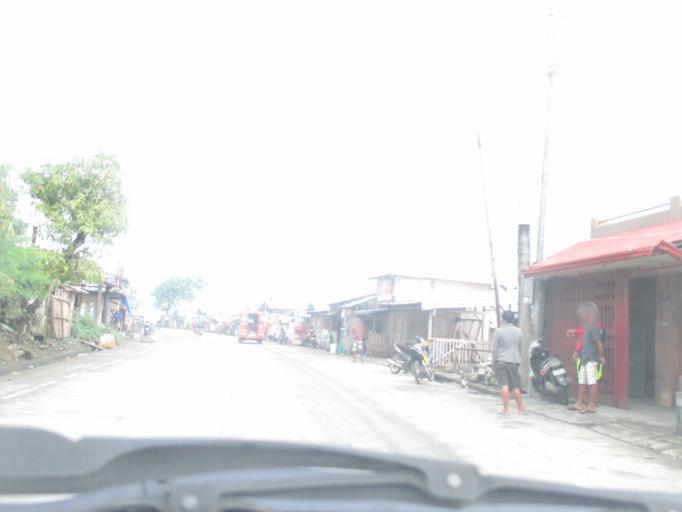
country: PH
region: Eastern Visayas
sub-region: Province of Leyte
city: Panalanoy
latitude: 11.2487
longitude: 124.9939
